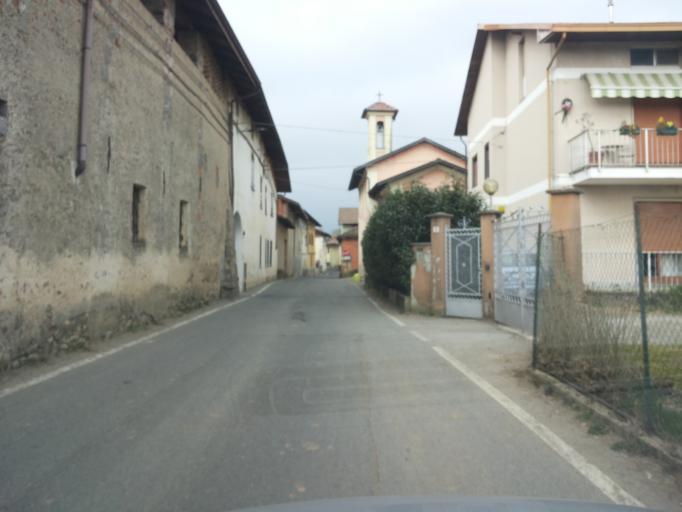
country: IT
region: Piedmont
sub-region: Provincia di Biella
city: Vergnasco
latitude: 45.4727
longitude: 8.0870
